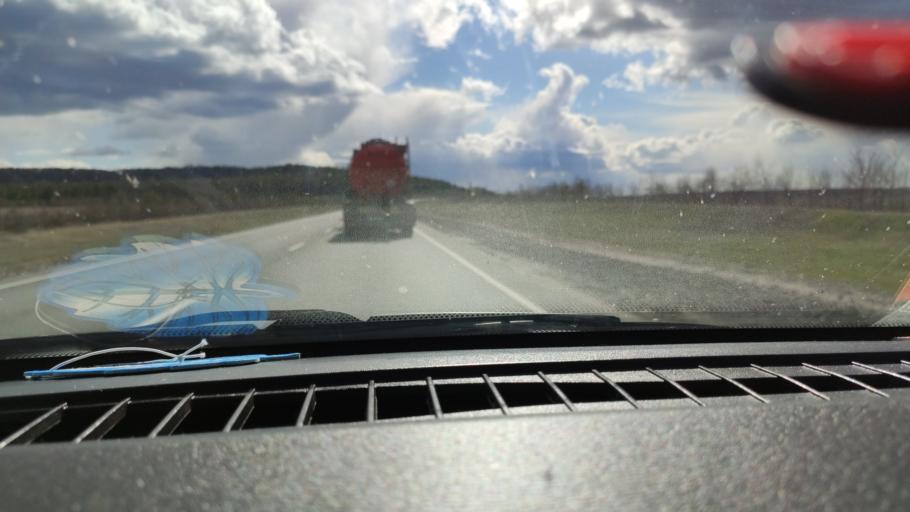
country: RU
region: Saratov
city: Khvalynsk
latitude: 52.5443
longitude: 48.0646
